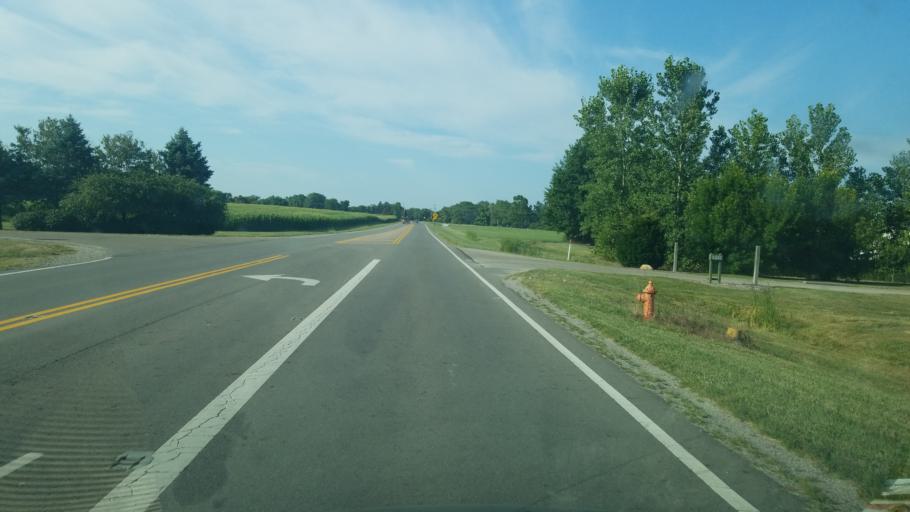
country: US
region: Ohio
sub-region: Franklin County
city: Lincoln Village
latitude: 39.9090
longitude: -83.1442
